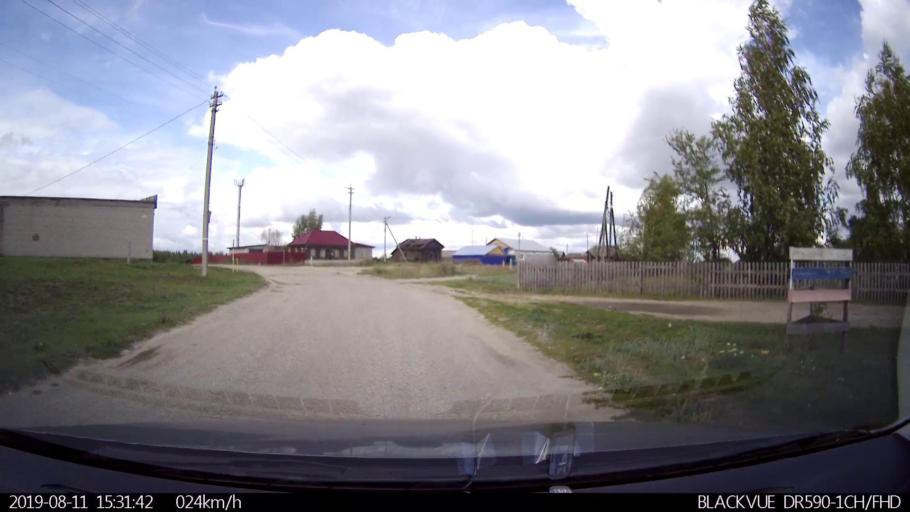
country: RU
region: Ulyanovsk
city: Ignatovka
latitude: 53.8581
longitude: 47.5760
